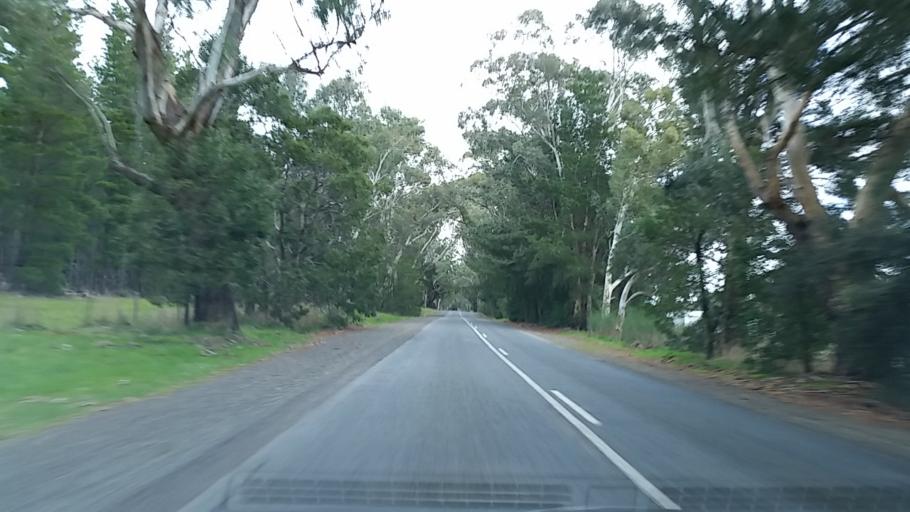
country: AU
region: South Australia
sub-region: Mount Barker
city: Meadows
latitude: -35.2362
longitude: 138.6778
